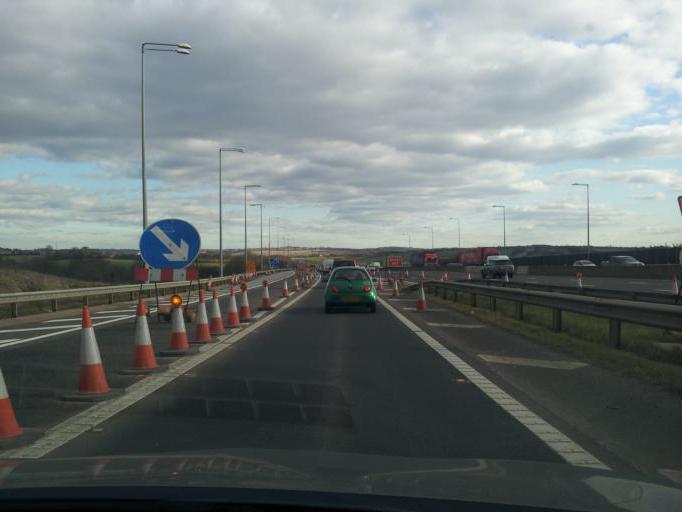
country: GB
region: England
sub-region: Derbyshire
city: Pinxton
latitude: 53.0989
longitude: -1.3190
